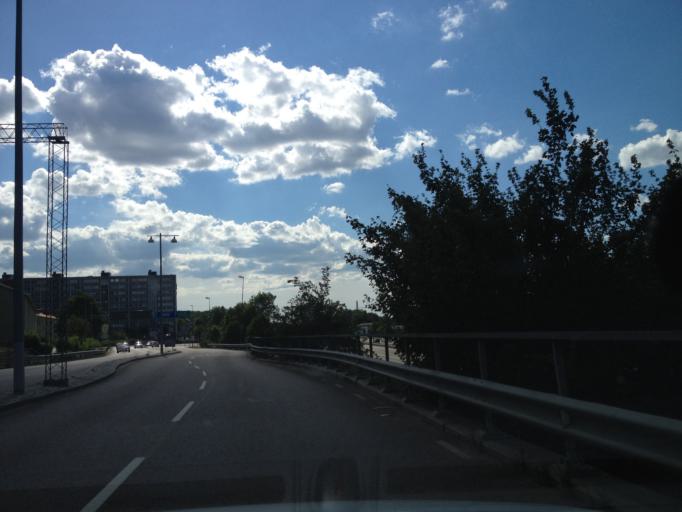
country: SE
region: Vaestra Goetaland
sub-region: Partille Kommun
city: Partille
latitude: 57.7366
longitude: 12.1000
